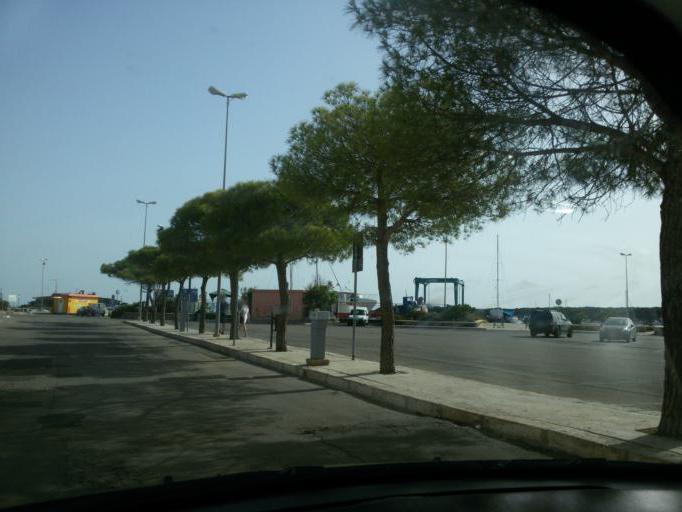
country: IT
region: Apulia
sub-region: Provincia di Lecce
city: Porto Cesareo
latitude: 40.2626
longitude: 17.8882
